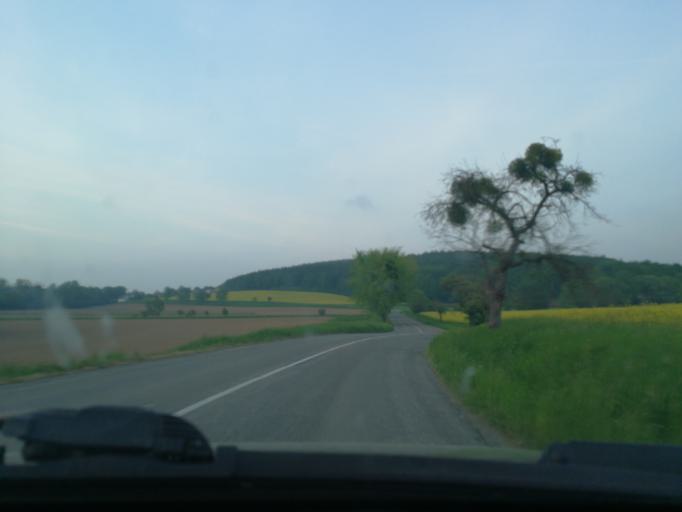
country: CZ
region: Zlin
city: Tecovice
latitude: 49.2478
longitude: 17.5687
